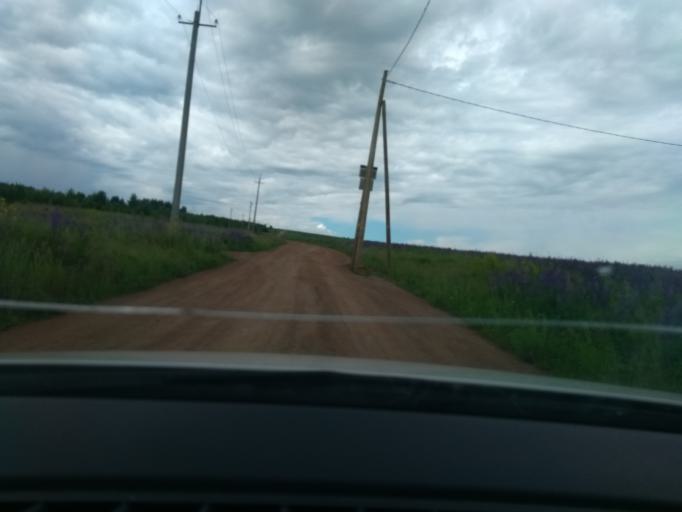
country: RU
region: Perm
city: Sylva
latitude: 57.8421
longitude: 56.7928
